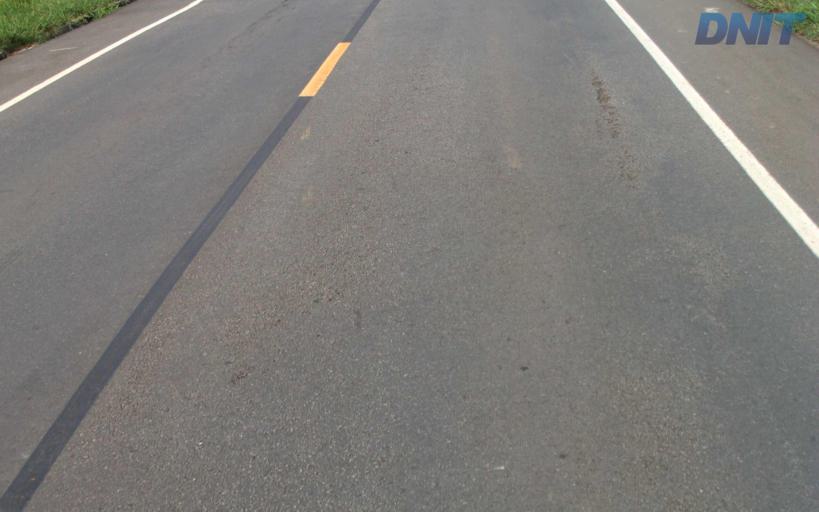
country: BR
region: Minas Gerais
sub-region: Belo Oriente
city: Belo Oriente
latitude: -19.2048
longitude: -42.2950
